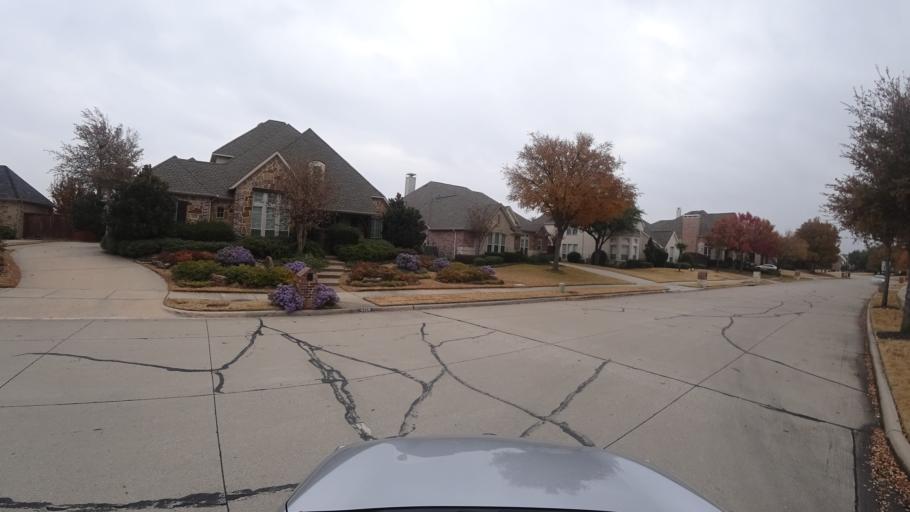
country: US
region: Texas
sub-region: Denton County
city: Lewisville
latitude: 33.0333
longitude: -96.9352
